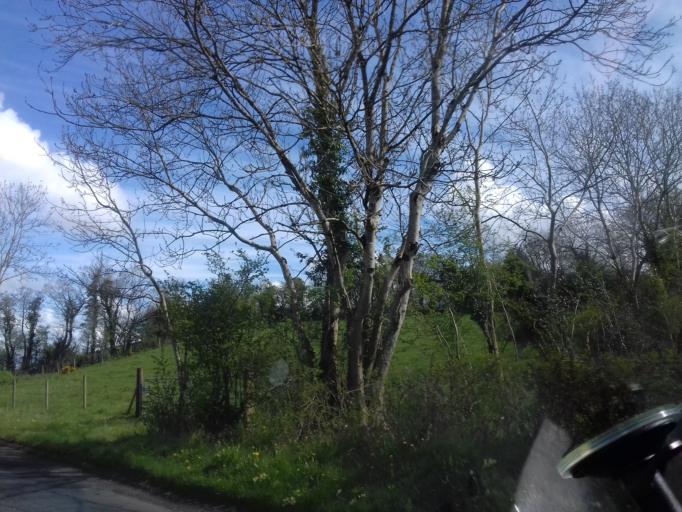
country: IE
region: Ulster
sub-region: An Cabhan
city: Belturbet
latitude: 54.1743
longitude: -7.5048
